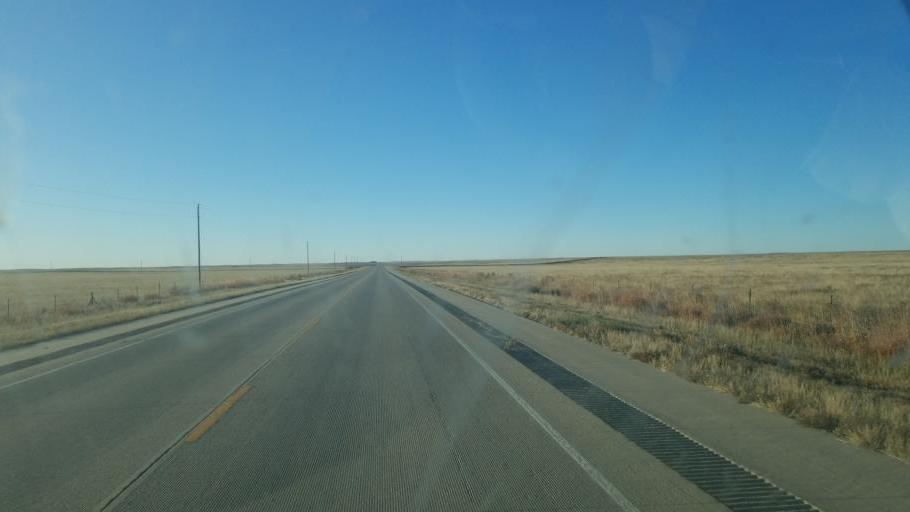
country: US
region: Colorado
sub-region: Kiowa County
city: Eads
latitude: 38.6487
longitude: -102.7859
